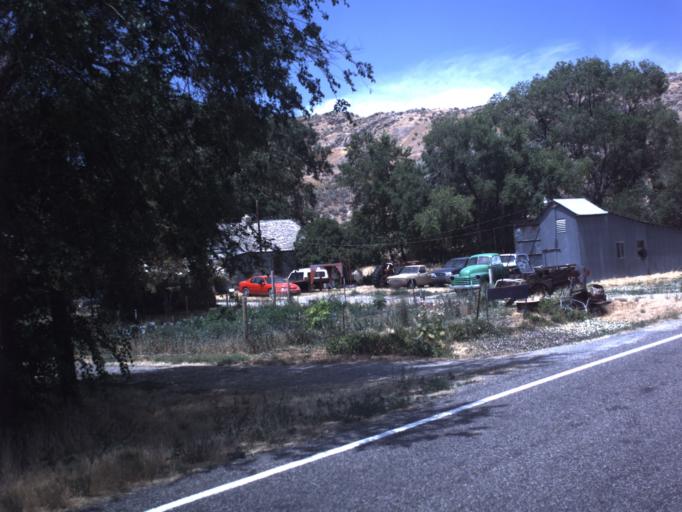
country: US
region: Utah
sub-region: Box Elder County
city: Tremonton
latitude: 41.6343
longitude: -112.3308
